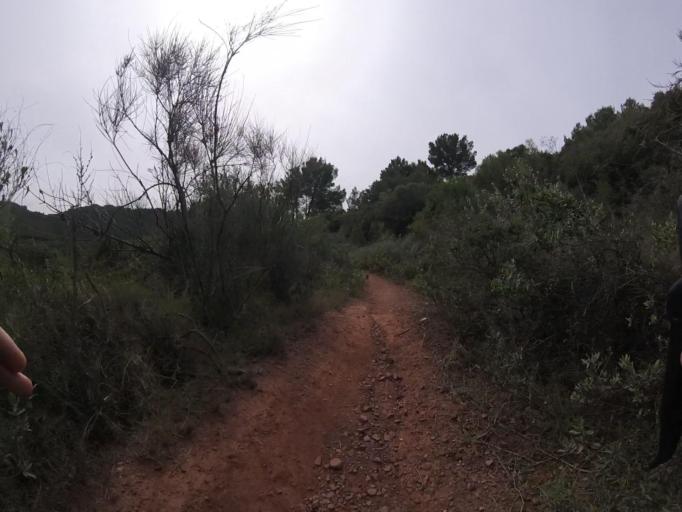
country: ES
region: Valencia
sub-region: Provincia de Castello
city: Benicassim
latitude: 40.0734
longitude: 0.0353
